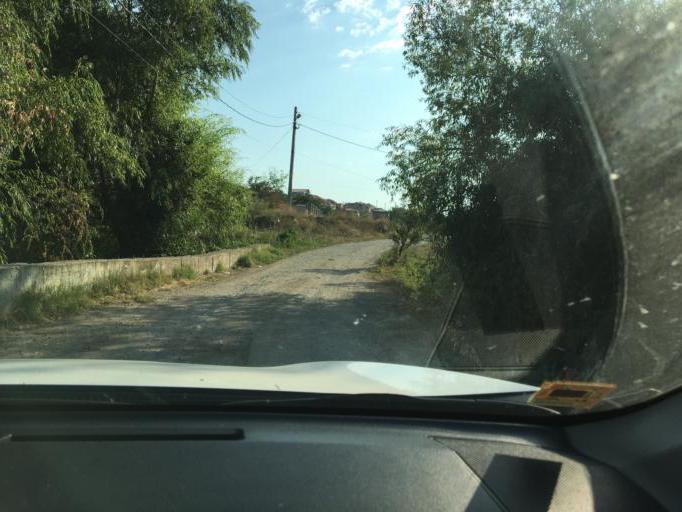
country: BG
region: Burgas
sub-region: Obshtina Burgas
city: Burgas
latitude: 42.6156
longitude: 27.4822
